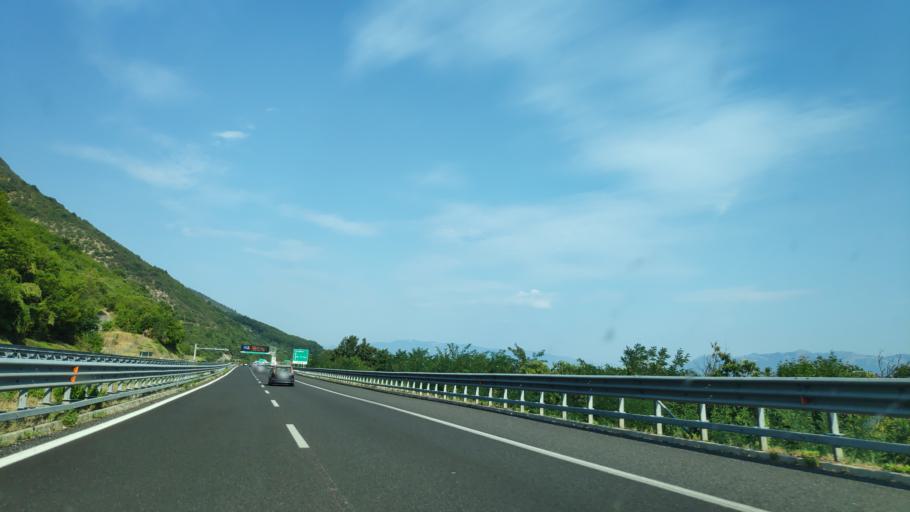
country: IT
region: Campania
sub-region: Provincia di Salerno
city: Auletta
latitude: 40.5513
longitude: 15.4053
